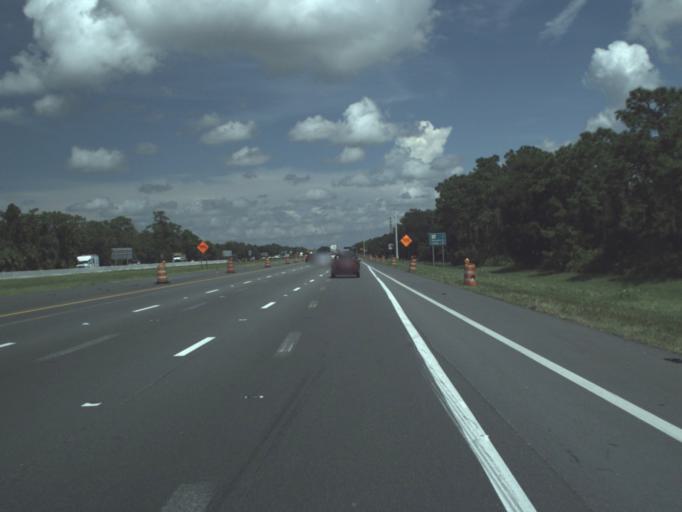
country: US
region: Florida
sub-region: Sarasota County
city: The Meadows
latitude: 27.4014
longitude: -82.4521
